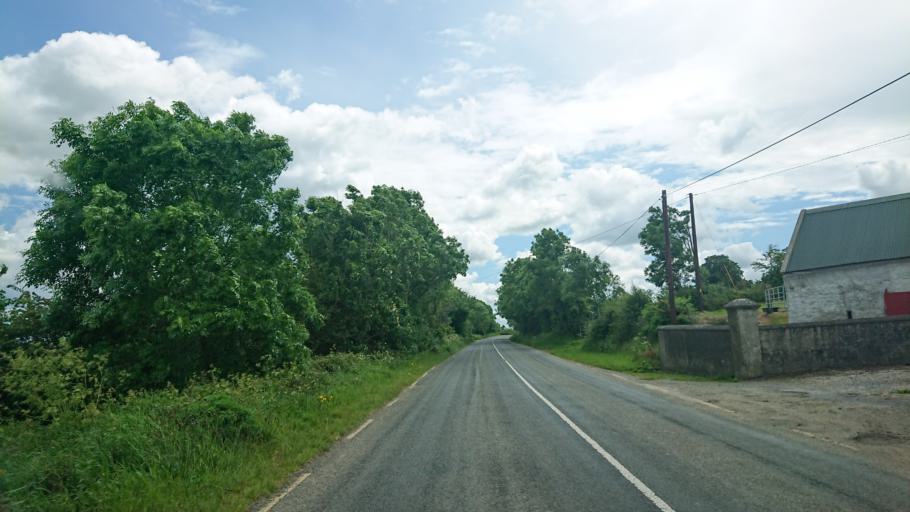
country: IE
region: Leinster
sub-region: Kilkenny
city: Graiguenamanagh
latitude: 52.4880
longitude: -6.9425
